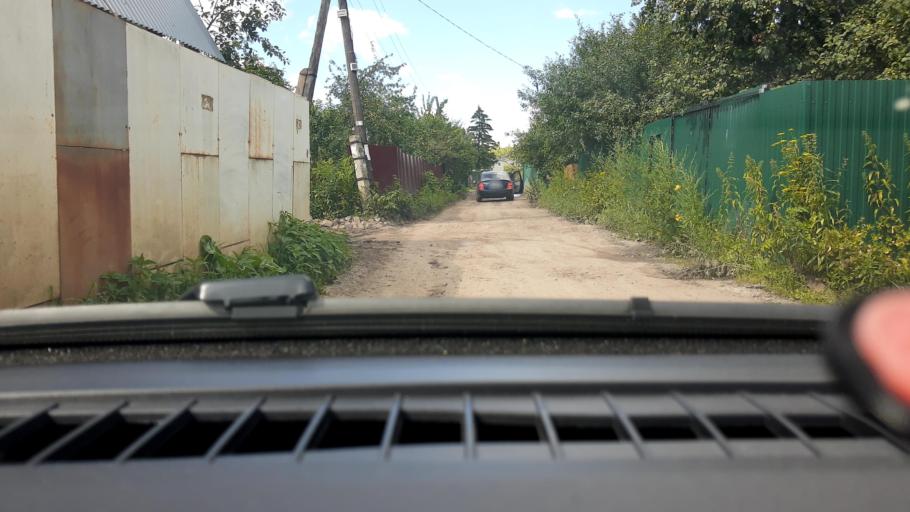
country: RU
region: Nizjnij Novgorod
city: Gorbatovka
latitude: 56.3184
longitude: 43.8291
